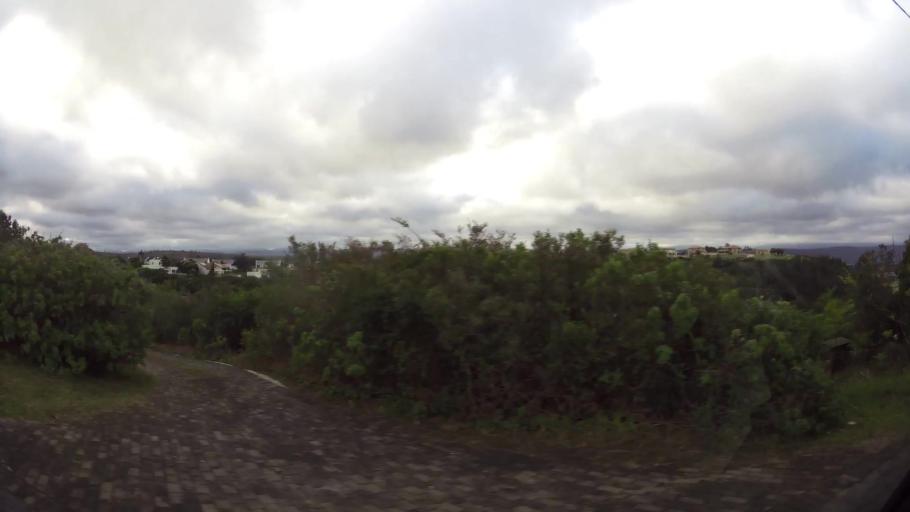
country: ZA
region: Western Cape
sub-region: Eden District Municipality
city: Plettenberg Bay
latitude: -34.0463
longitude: 23.3642
